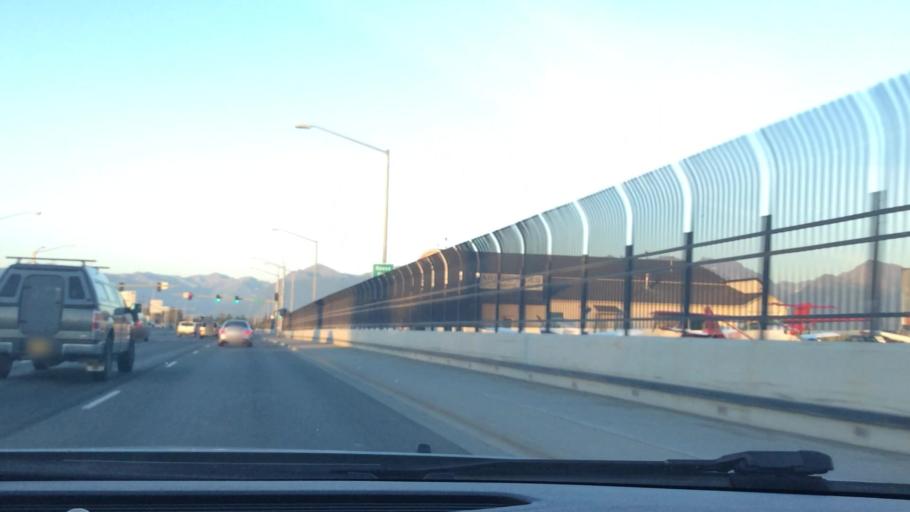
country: US
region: Alaska
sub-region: Anchorage Municipality
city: Anchorage
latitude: 61.2174
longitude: -149.8396
